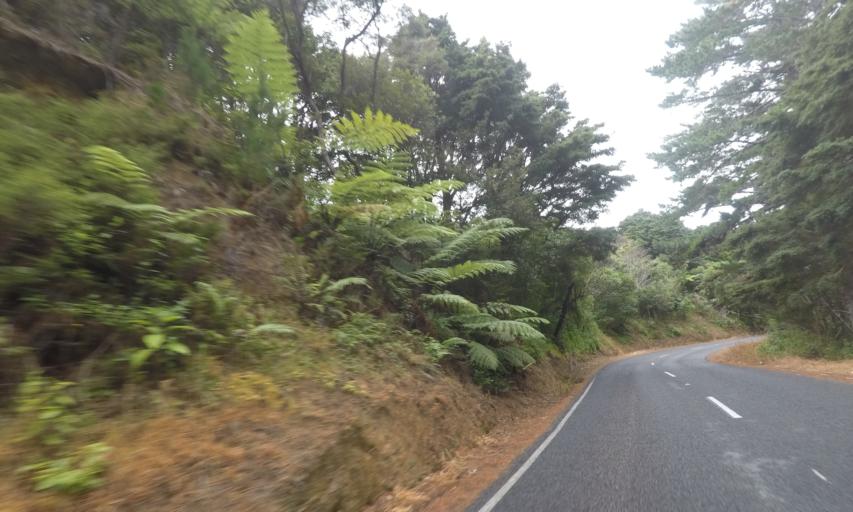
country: NZ
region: Northland
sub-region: Whangarei
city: Whangarei
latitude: -35.7620
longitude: 174.4577
